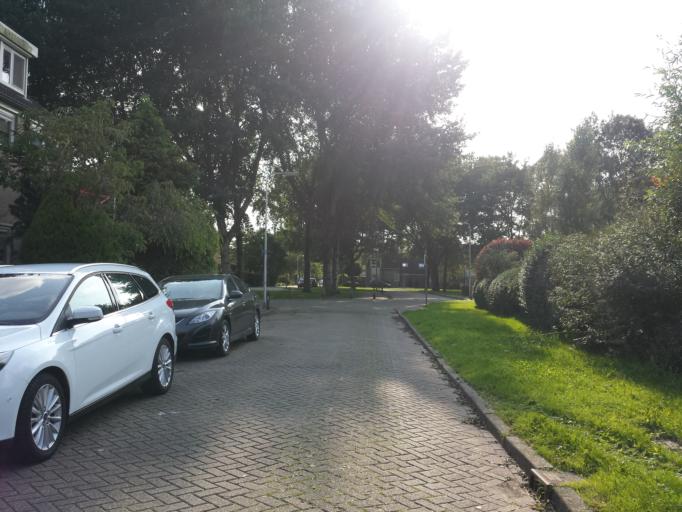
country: NL
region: South Holland
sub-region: Gemeente Waddinxveen
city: Groenswaard
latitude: 52.0393
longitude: 4.6337
